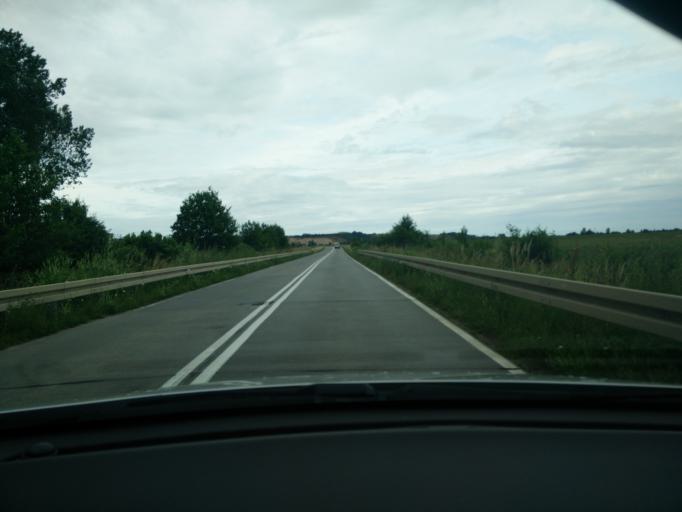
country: PL
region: Pomeranian Voivodeship
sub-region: Powiat pucki
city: Mrzezino
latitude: 54.6347
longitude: 18.4390
